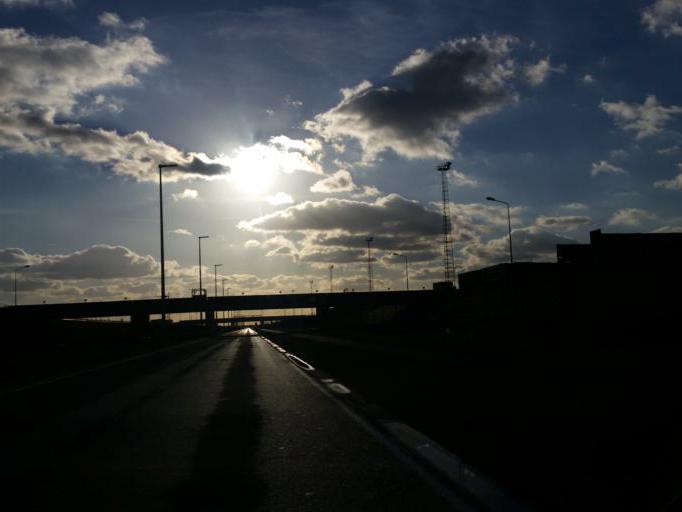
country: BE
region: Flanders
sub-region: Provincie Oost-Vlaanderen
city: Beveren
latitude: 51.2936
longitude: 4.2501
